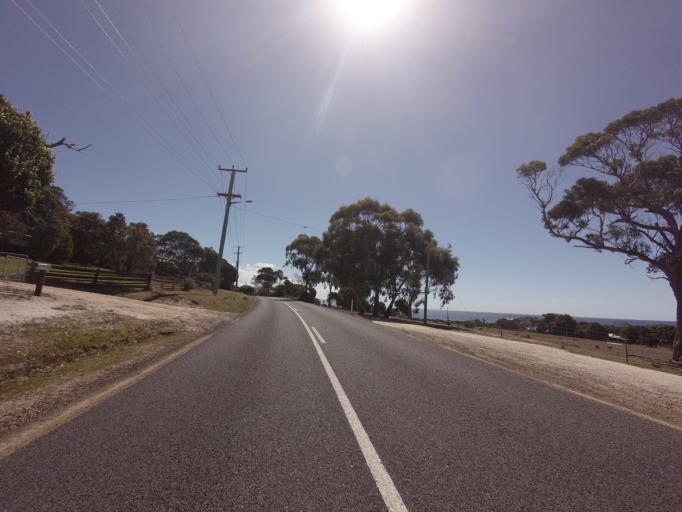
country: AU
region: Tasmania
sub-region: Break O'Day
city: St Helens
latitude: -41.8643
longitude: 148.2828
